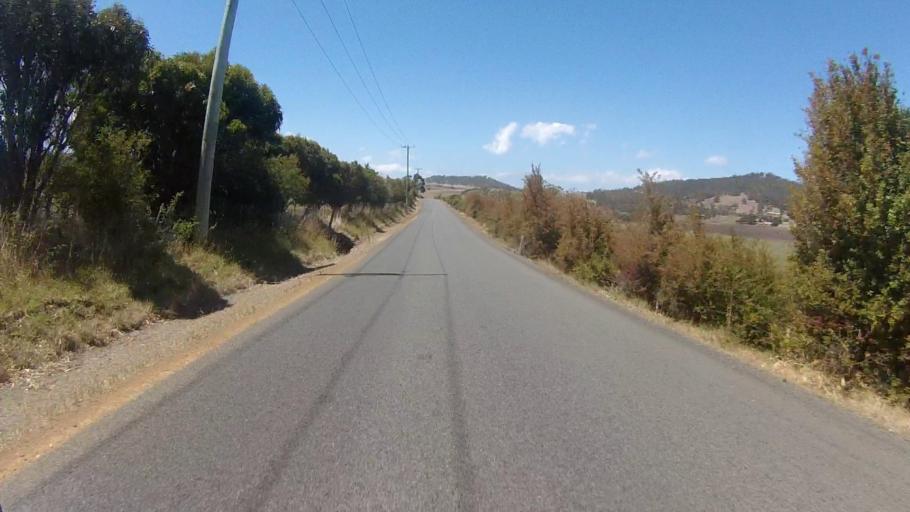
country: AU
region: Tasmania
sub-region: Sorell
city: Sorell
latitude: -42.7725
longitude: 147.5881
